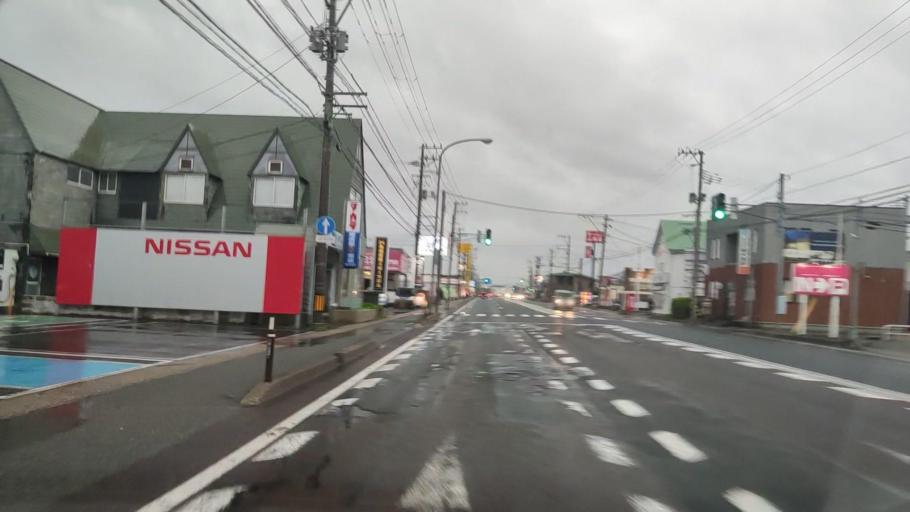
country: JP
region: Akita
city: Akita
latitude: 39.6879
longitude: 140.1244
